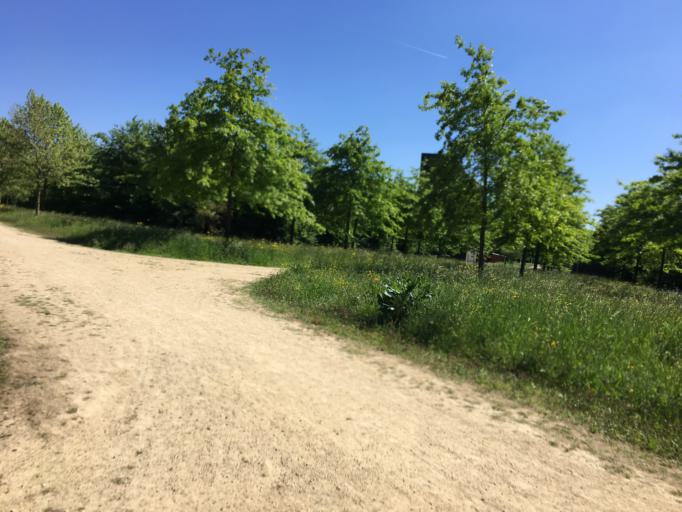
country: NL
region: Gelderland
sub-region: Gemeente Maasdriel
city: Hedel
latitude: 51.7277
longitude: 5.2458
